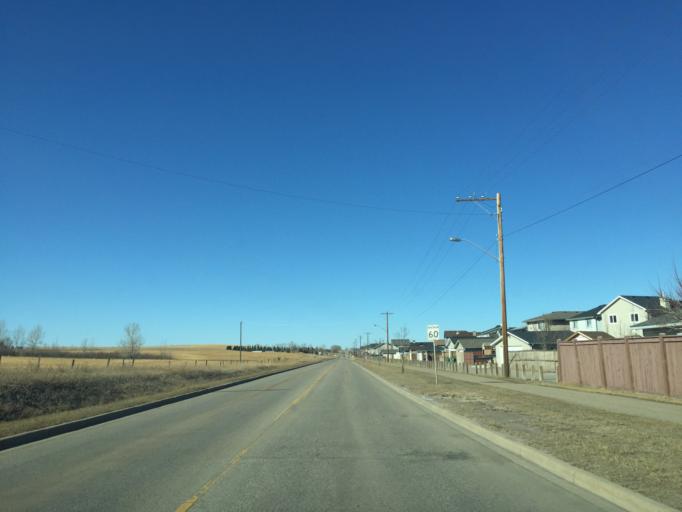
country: CA
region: Alberta
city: Airdrie
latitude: 51.2884
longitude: -114.0485
